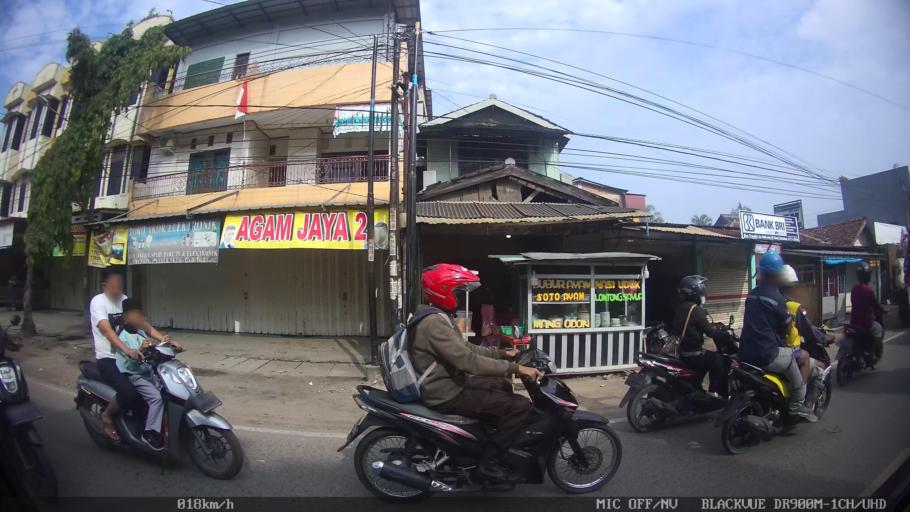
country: ID
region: Lampung
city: Panjang
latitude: -5.4708
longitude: 105.3223
